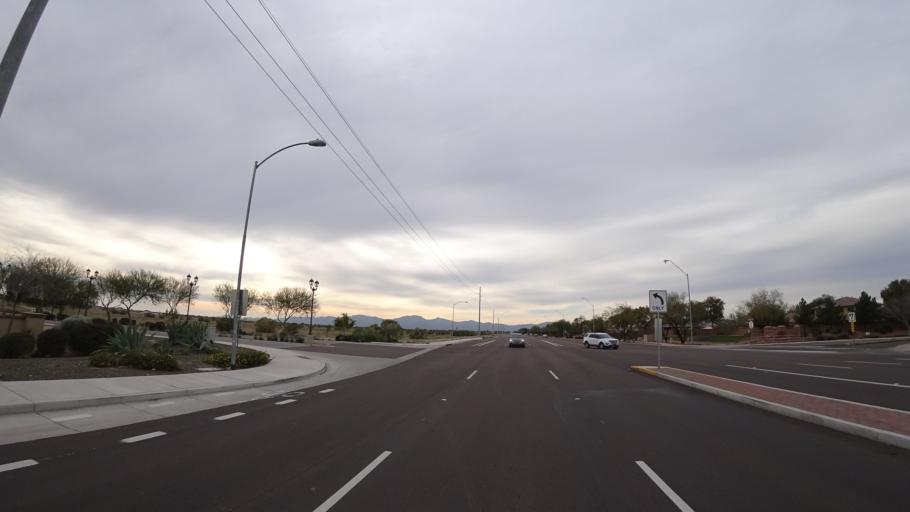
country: US
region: Arizona
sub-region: Maricopa County
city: Surprise
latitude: 33.6091
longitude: -112.3632
